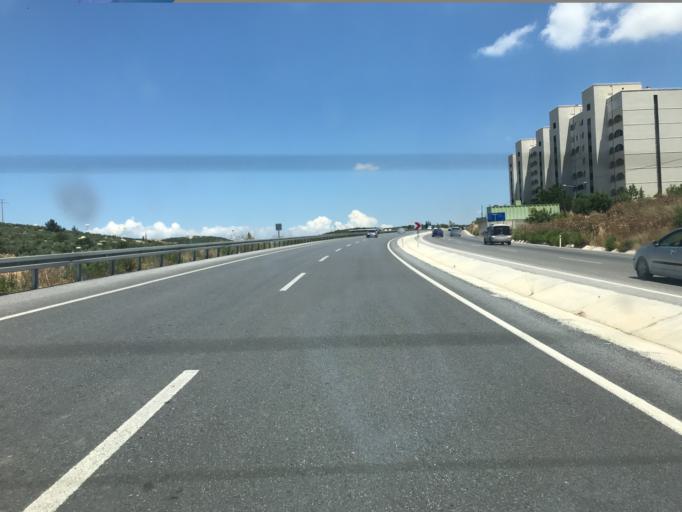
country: TR
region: Aydin
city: Akkoy
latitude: 37.4747
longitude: 27.3396
